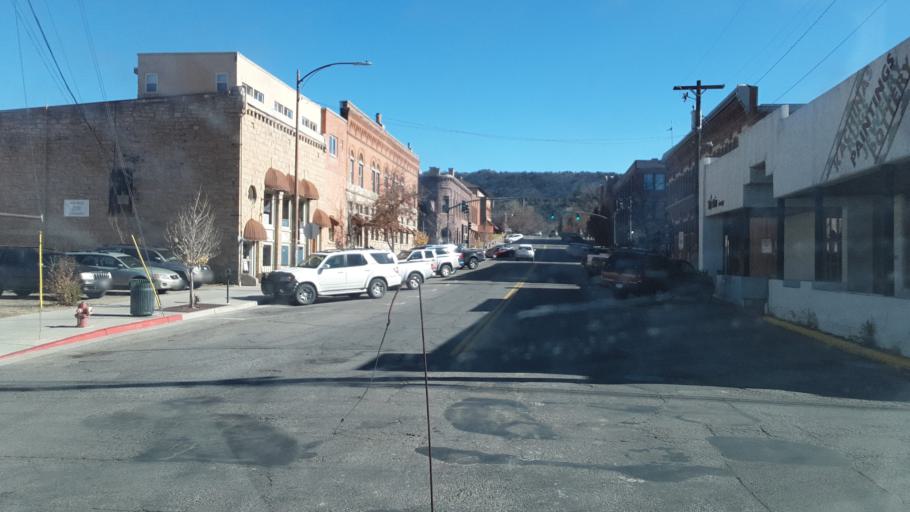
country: US
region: Colorado
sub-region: La Plata County
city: Durango
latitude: 37.2736
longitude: -107.8817
